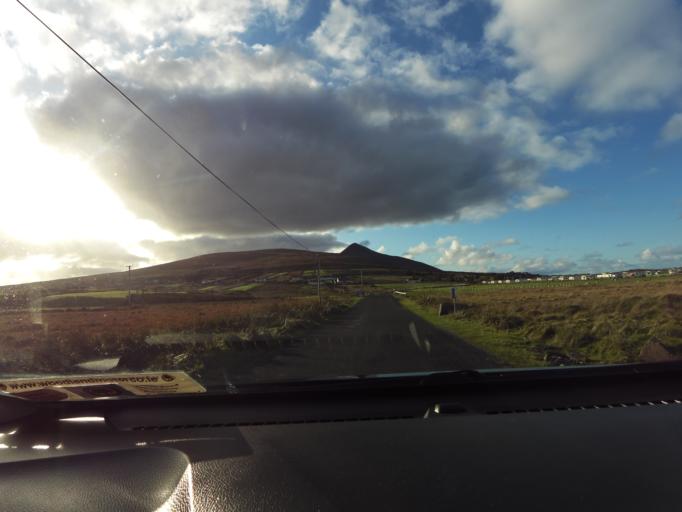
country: IE
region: Connaught
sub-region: Maigh Eo
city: Belmullet
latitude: 54.0095
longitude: -9.9870
